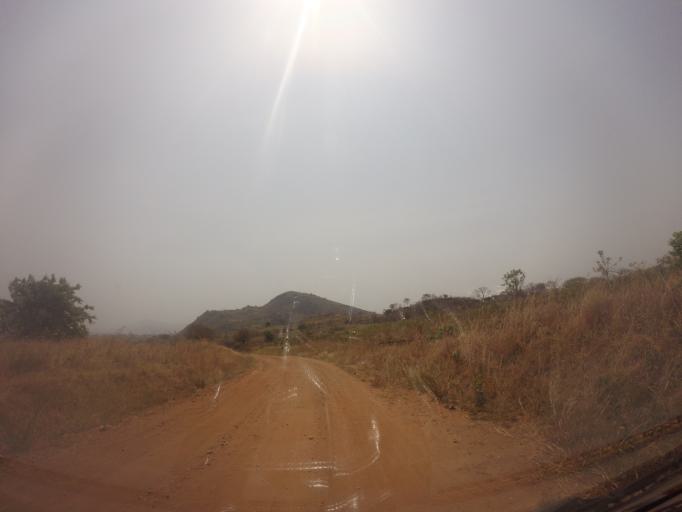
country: UG
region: Northern Region
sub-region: Arua District
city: Arua
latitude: 2.9264
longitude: 30.9821
